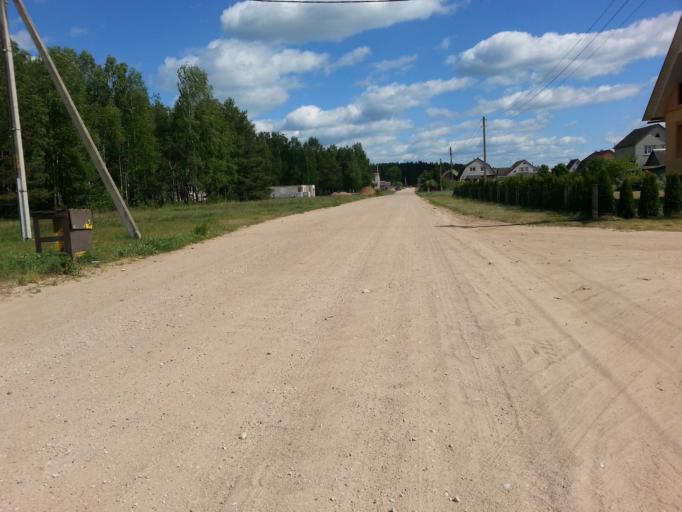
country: BY
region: Minsk
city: Narach
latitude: 54.9271
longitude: 26.6847
